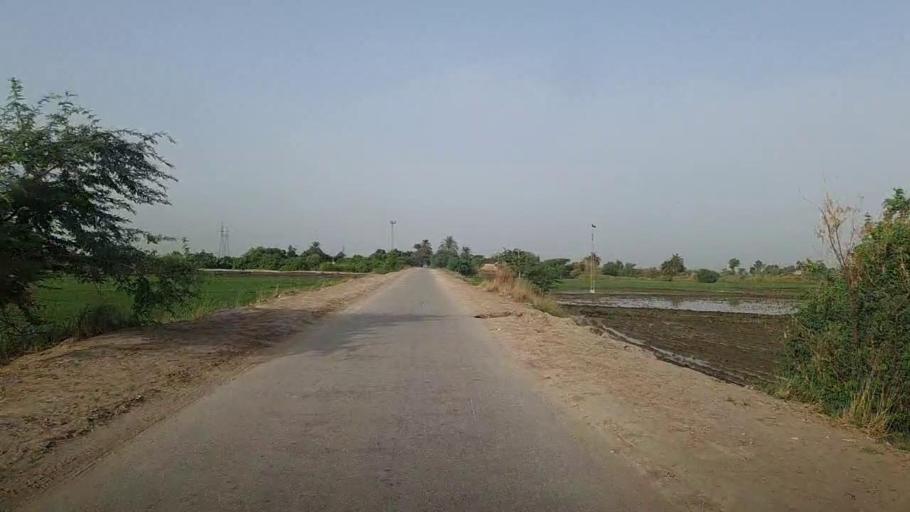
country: PK
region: Sindh
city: Mehar
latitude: 27.1502
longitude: 67.8005
